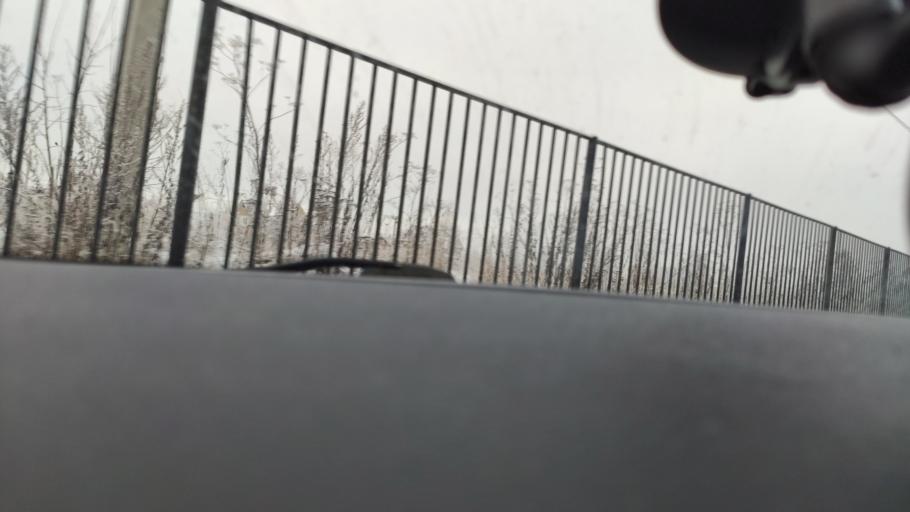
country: RU
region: Perm
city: Perm
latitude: 58.0455
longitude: 56.3679
